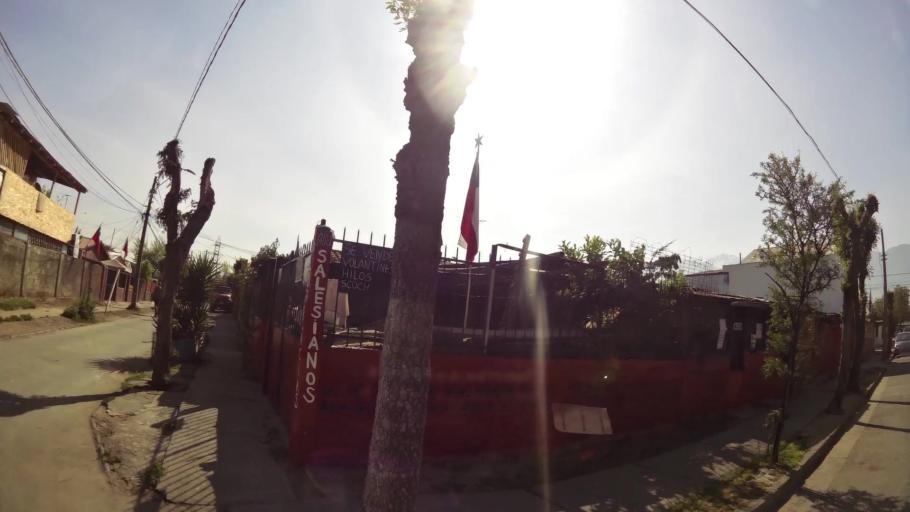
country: CL
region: Santiago Metropolitan
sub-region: Provincia de Santiago
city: Villa Presidente Frei, Nunoa, Santiago, Chile
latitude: -33.5022
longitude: -70.5856
